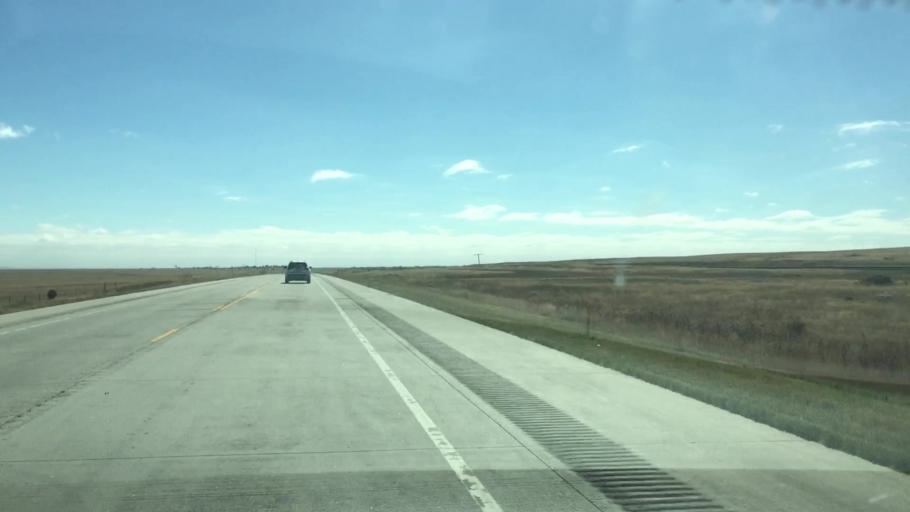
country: US
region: Colorado
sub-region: Lincoln County
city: Hugo
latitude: 39.1703
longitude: -103.5312
